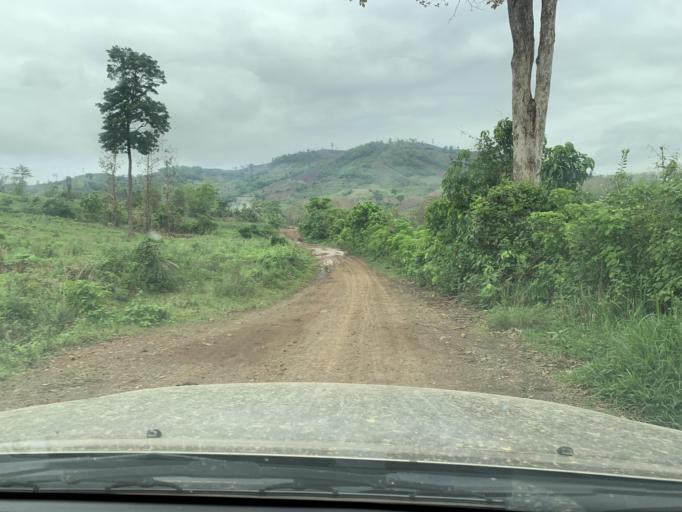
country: TH
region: Uttaradit
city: Ban Khok
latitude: 18.3968
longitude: 101.4298
